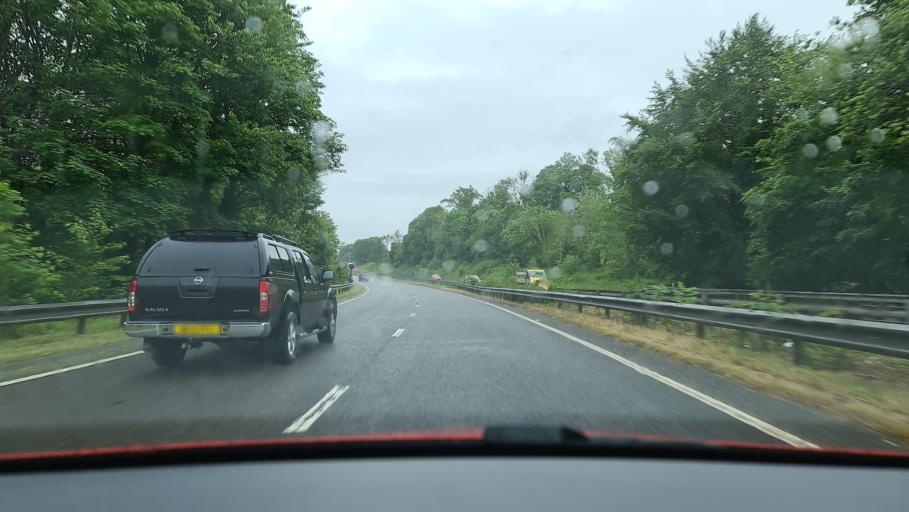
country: GB
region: England
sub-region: Cornwall
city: Liskeard
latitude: 50.4504
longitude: -4.4821
